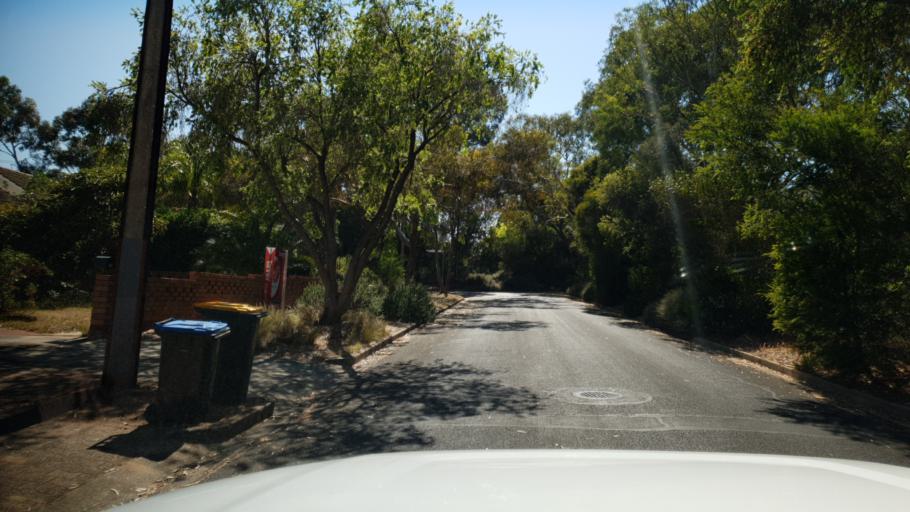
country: AU
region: South Australia
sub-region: Mitcham
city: Clapham
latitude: -34.9954
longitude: 138.5885
